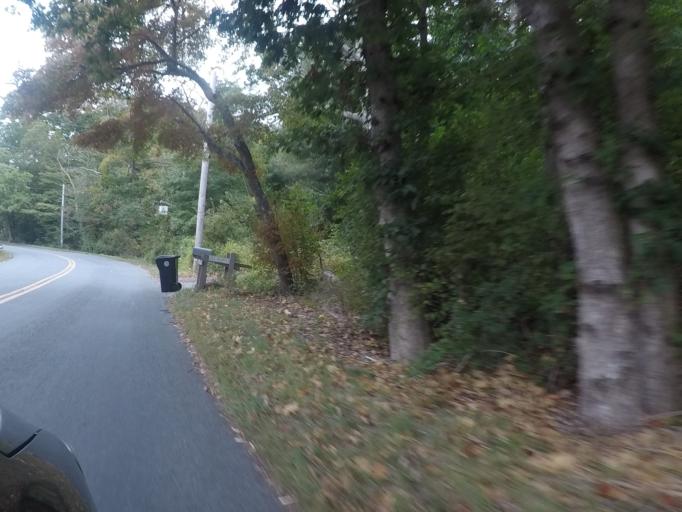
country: US
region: Massachusetts
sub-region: Bristol County
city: Smith Mills
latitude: 41.5698
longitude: -71.0060
